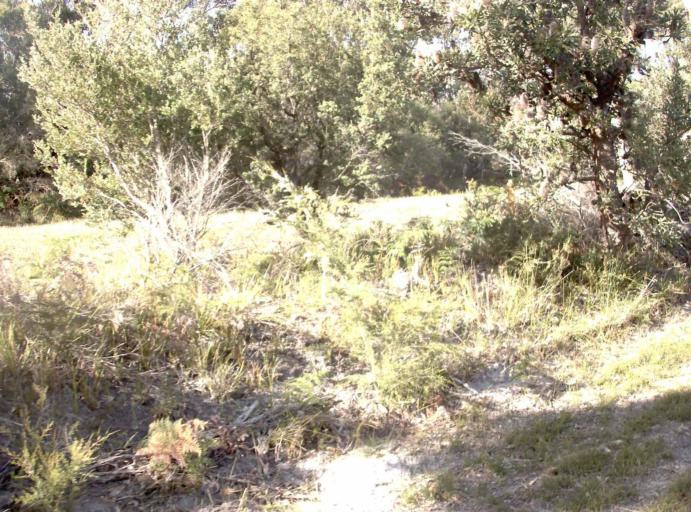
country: AU
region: Victoria
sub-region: East Gippsland
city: Lakes Entrance
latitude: -37.7992
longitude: 148.7363
